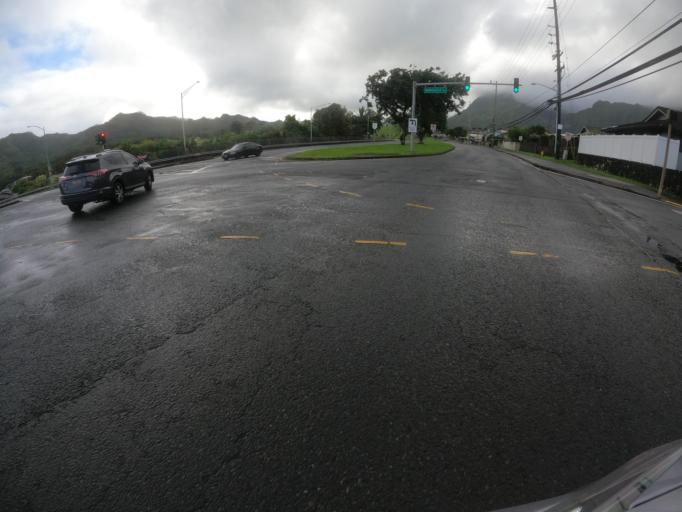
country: US
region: Hawaii
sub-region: Honolulu County
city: Kane'ohe
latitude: 21.3937
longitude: -157.7972
